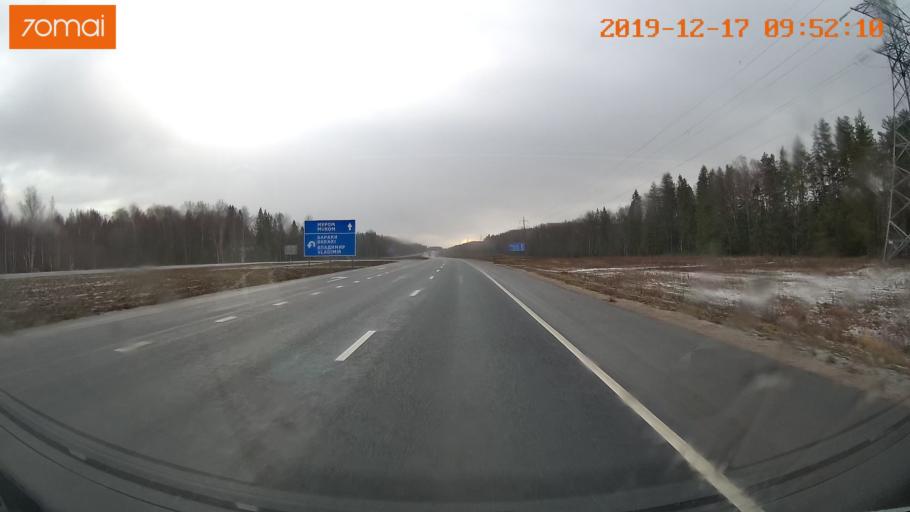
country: RU
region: Vladimir
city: Kommunar
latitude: 56.0357
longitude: 40.5336
